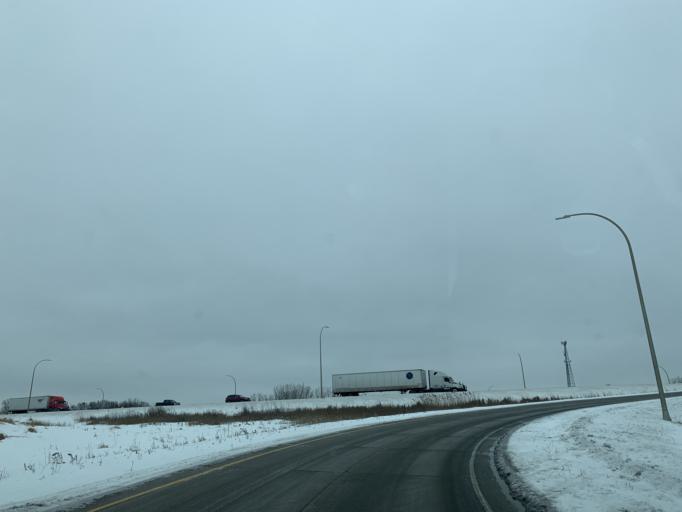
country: US
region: Minnesota
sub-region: Washington County
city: Birchwood
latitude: 45.0292
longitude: -92.9600
